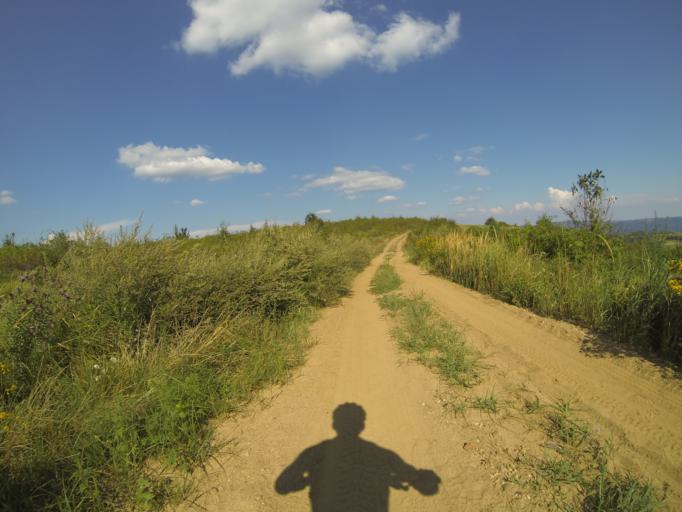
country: RO
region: Mehedinti
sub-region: Comuna Svinita
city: Svinita
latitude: 44.5625
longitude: 22.1512
